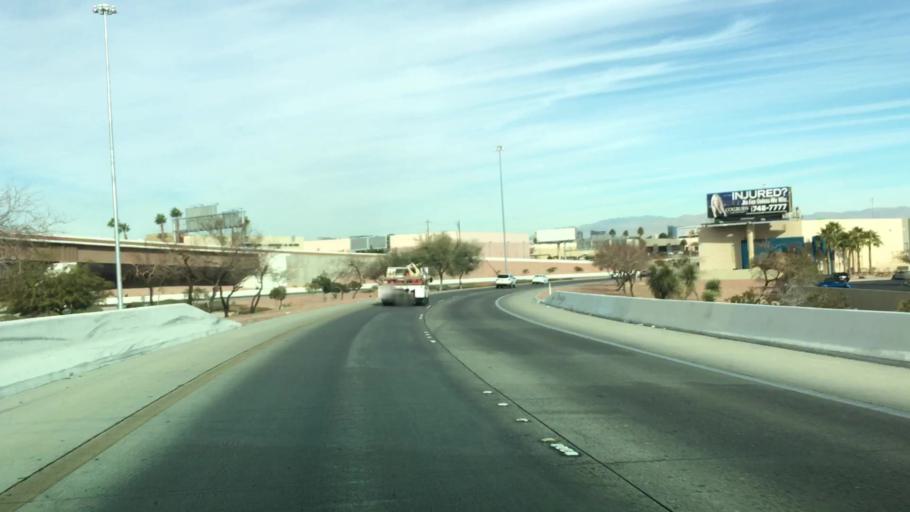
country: US
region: Nevada
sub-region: Clark County
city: Paradise
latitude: 36.0637
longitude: -115.1478
